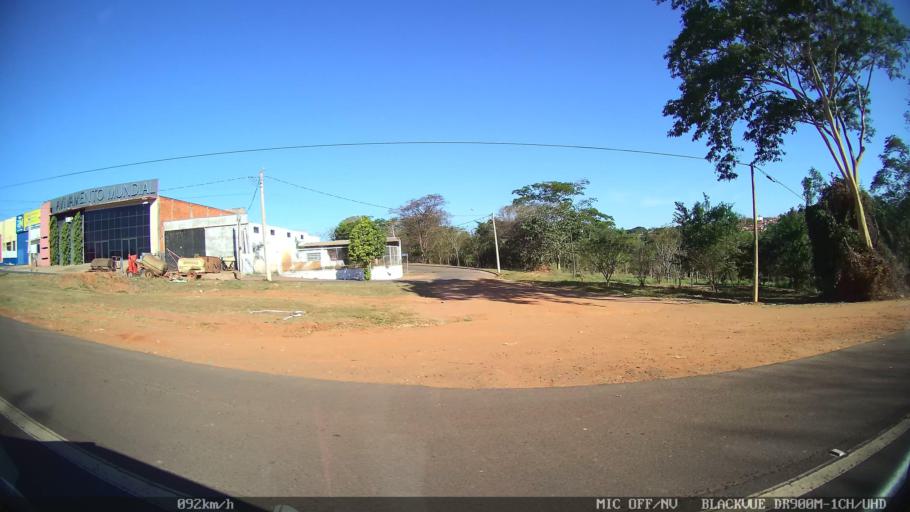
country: BR
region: Sao Paulo
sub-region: Olimpia
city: Olimpia
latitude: -20.7380
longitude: -48.8851
